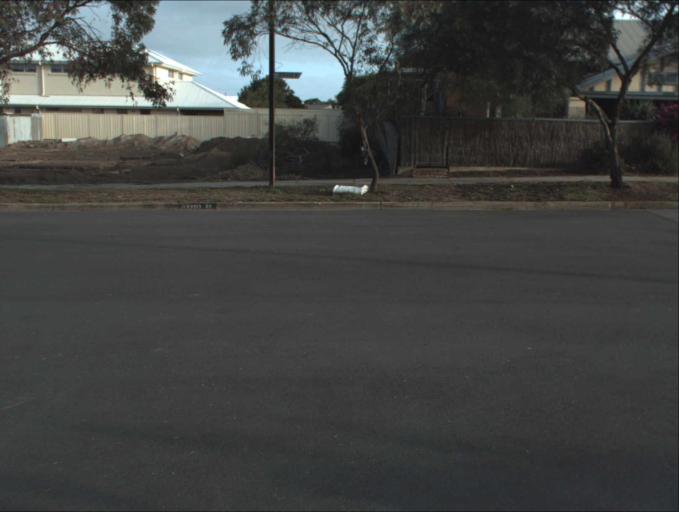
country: AU
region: South Australia
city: Port Adelaide
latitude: -34.8463
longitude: 138.4789
